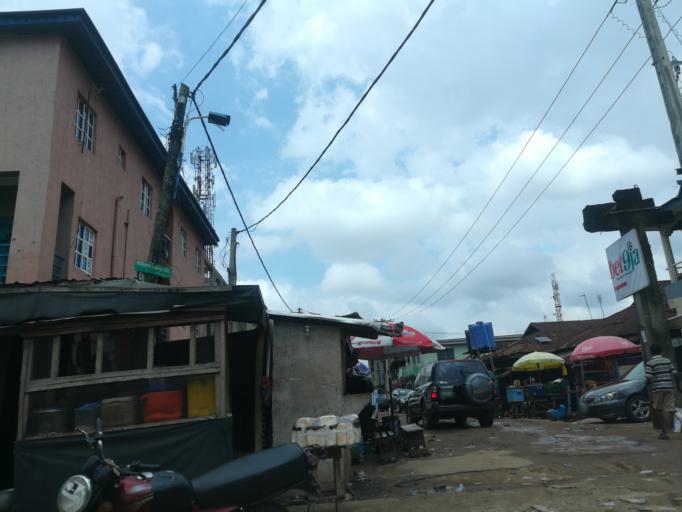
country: NG
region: Lagos
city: Mushin
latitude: 6.5306
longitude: 3.3568
